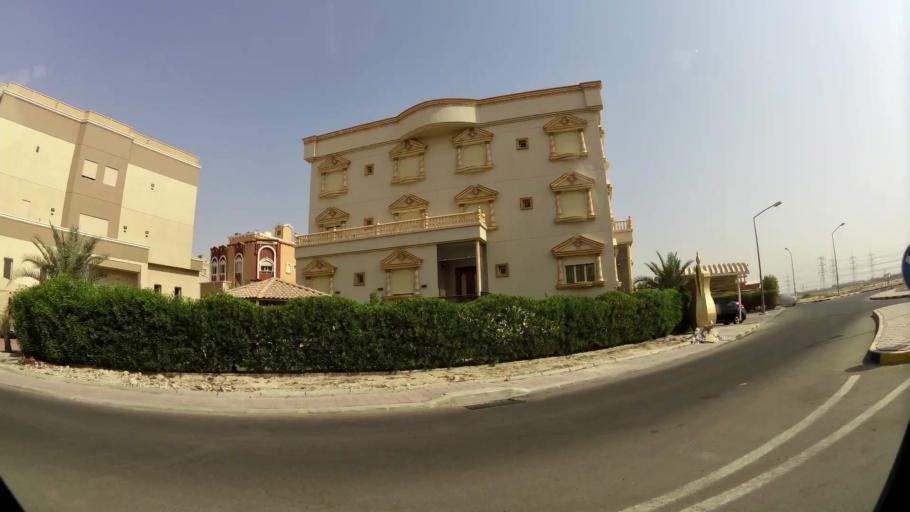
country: KW
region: Muhafazat al Jahra'
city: Al Jahra'
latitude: 29.3314
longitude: 47.7805
